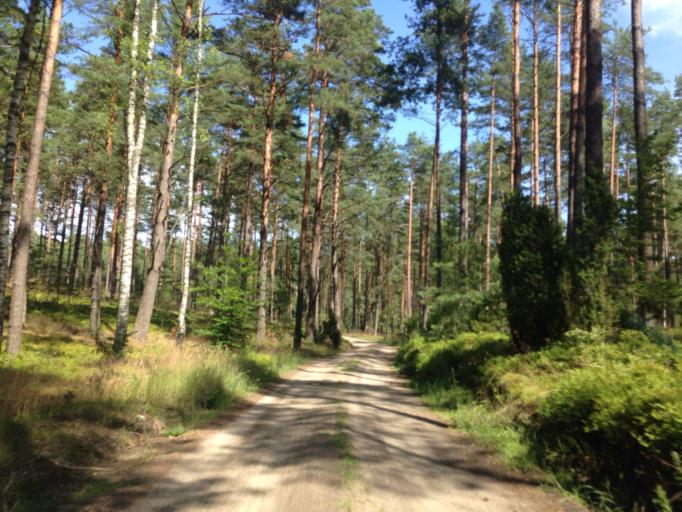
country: PL
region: Pomeranian Voivodeship
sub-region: Powiat koscierski
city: Dziemiany
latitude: 53.9820
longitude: 17.8224
